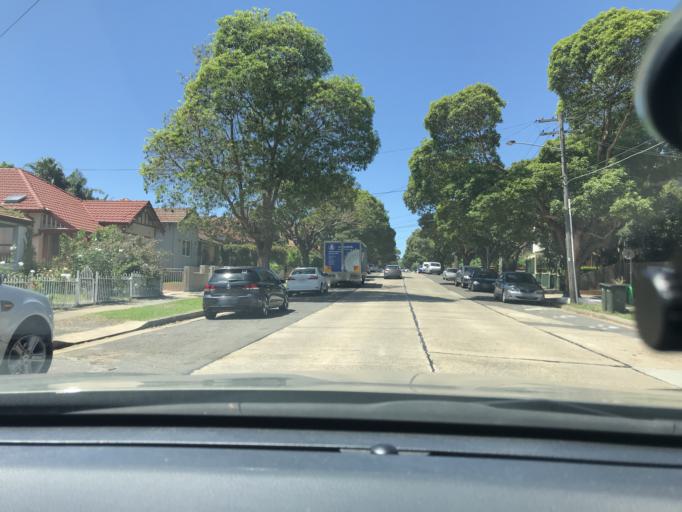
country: AU
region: New South Wales
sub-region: Canada Bay
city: Wareemba
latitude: -33.8677
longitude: 151.1229
